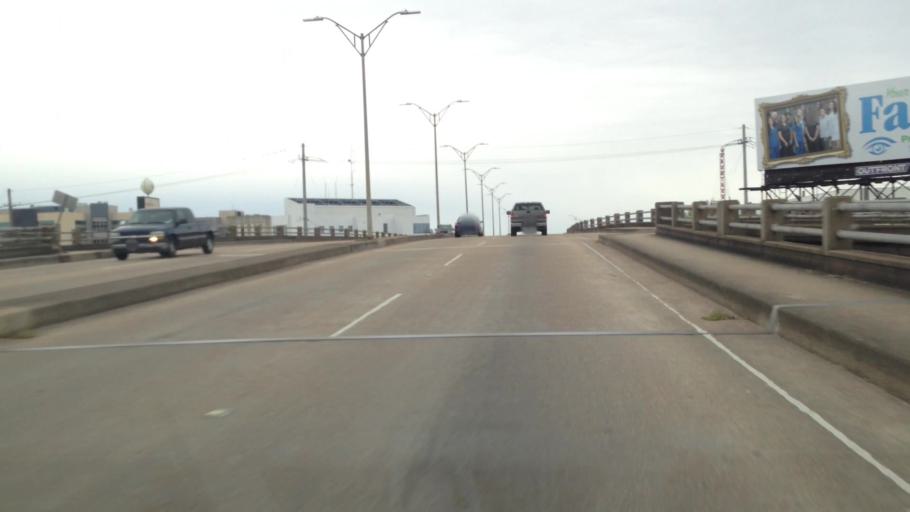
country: US
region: Louisiana
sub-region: Orleans Parish
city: New Orleans
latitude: 29.9552
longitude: -90.0960
